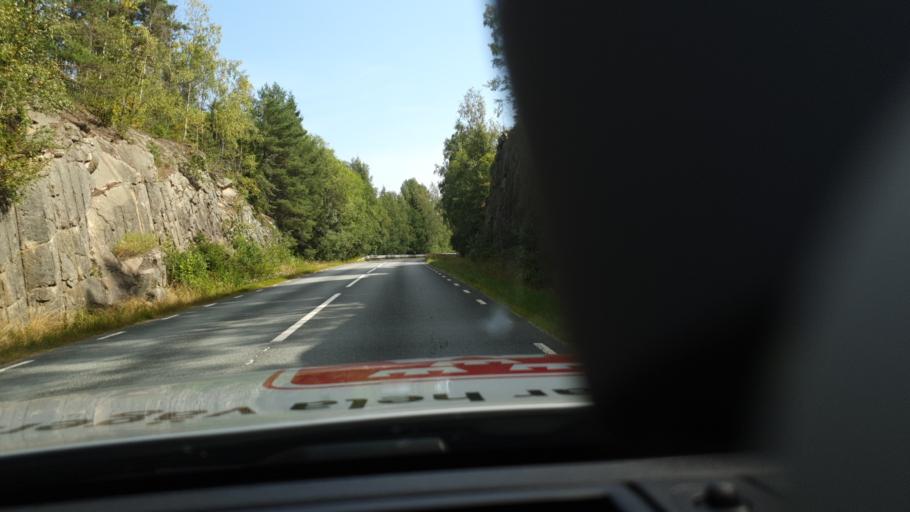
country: SE
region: Joenkoeping
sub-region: Vetlanda Kommun
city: Vetlanda
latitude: 57.3824
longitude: 15.2012
